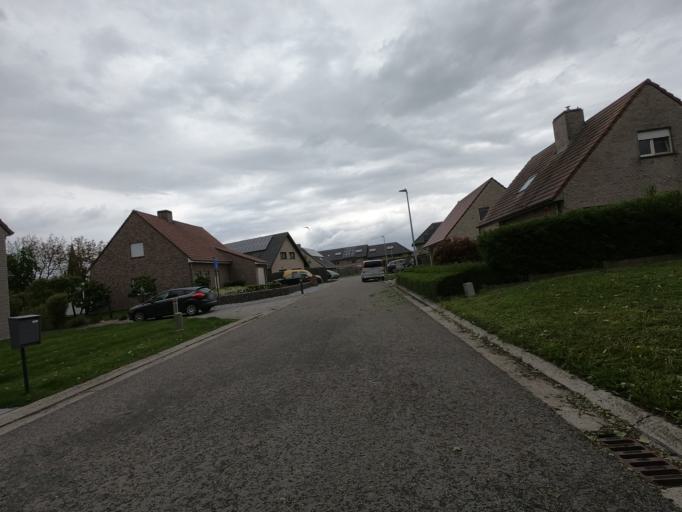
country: BE
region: Flanders
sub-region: Provincie West-Vlaanderen
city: Poperinge
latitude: 50.9315
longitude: 2.7418
